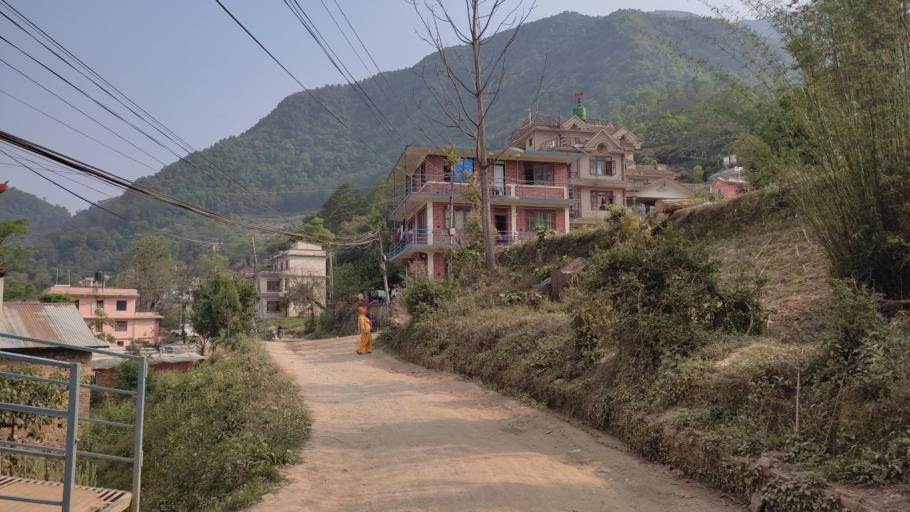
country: NP
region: Central Region
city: Kirtipur
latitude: 27.6630
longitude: 85.2581
